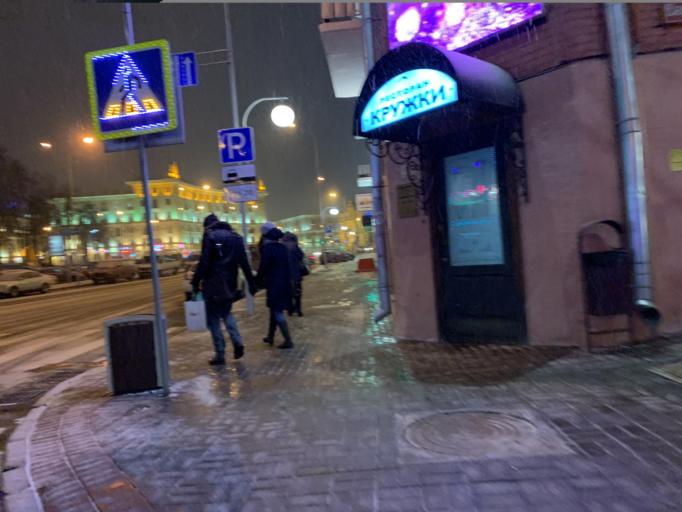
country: BY
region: Minsk
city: Minsk
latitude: 53.8948
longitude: 27.5547
